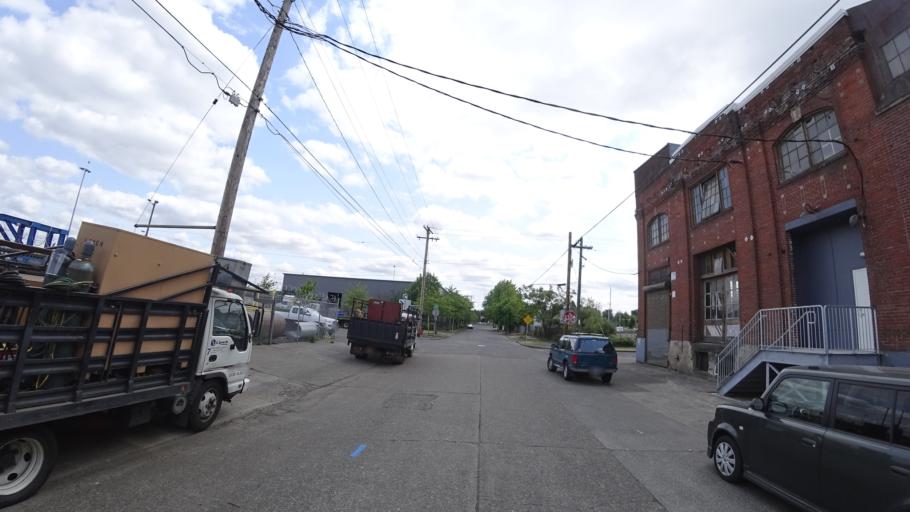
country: US
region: Oregon
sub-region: Clackamas County
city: Milwaukie
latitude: 45.4878
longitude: -122.6474
